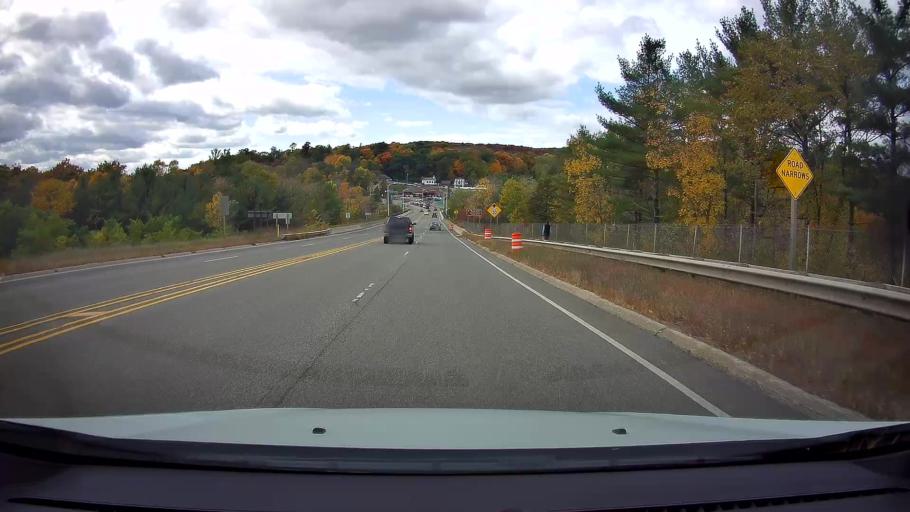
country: US
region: Wisconsin
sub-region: Polk County
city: Saint Croix Falls
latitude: 45.4023
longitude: -92.6475
